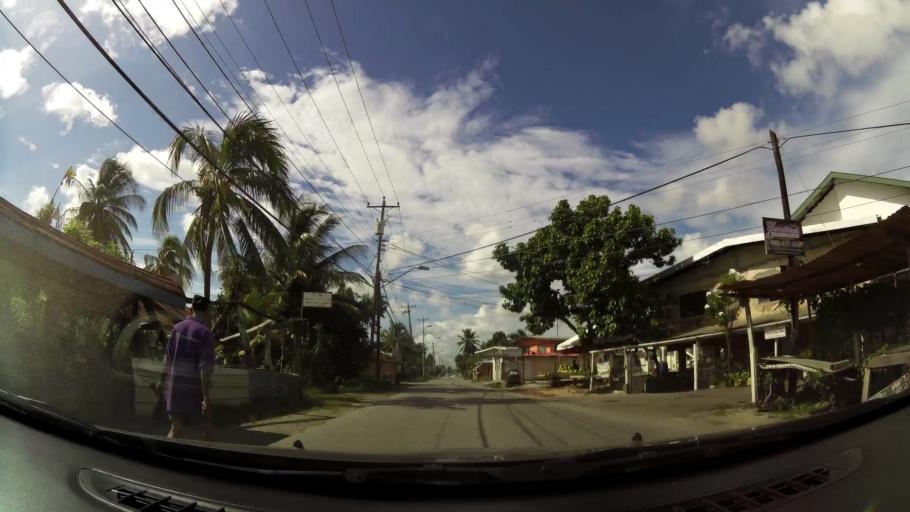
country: TT
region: Chaguanas
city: Chaguanas
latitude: 10.5291
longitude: -61.4054
